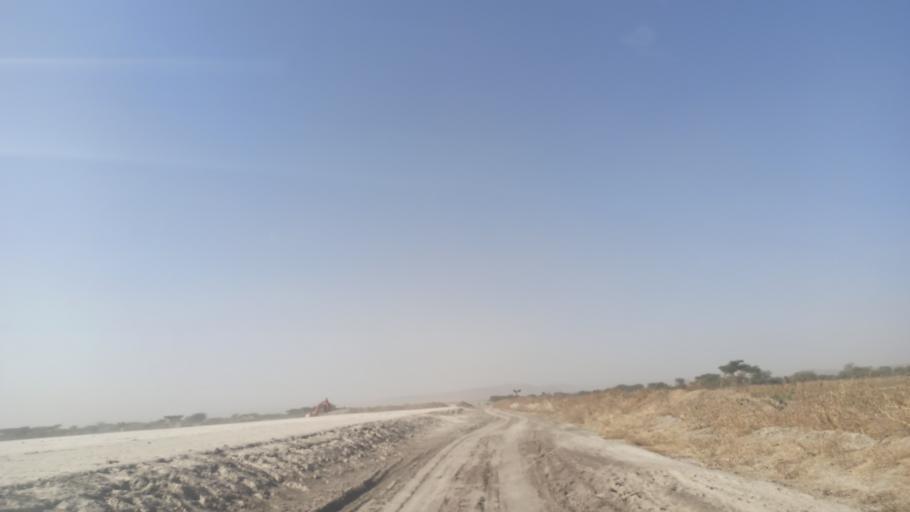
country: ET
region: Oromiya
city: Ziway
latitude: 7.7322
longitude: 38.6251
